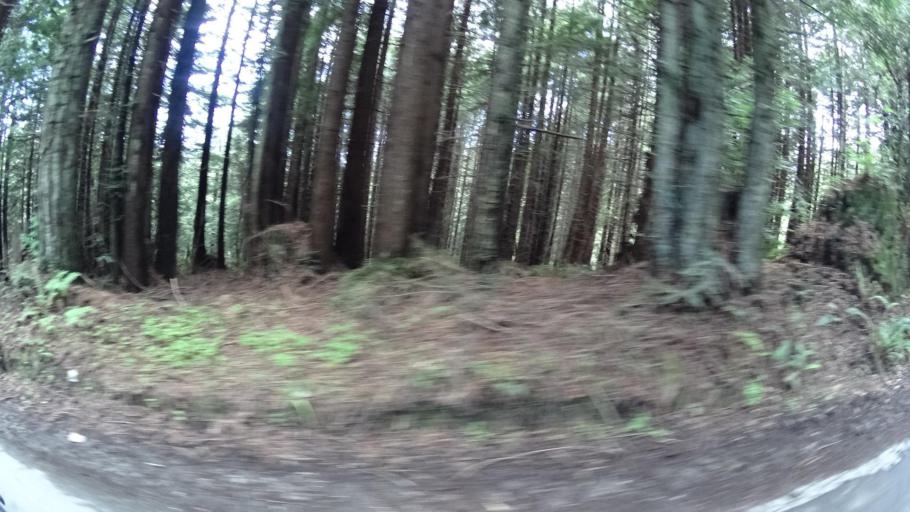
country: US
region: California
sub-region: Humboldt County
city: Blue Lake
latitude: 40.8989
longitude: -123.9984
